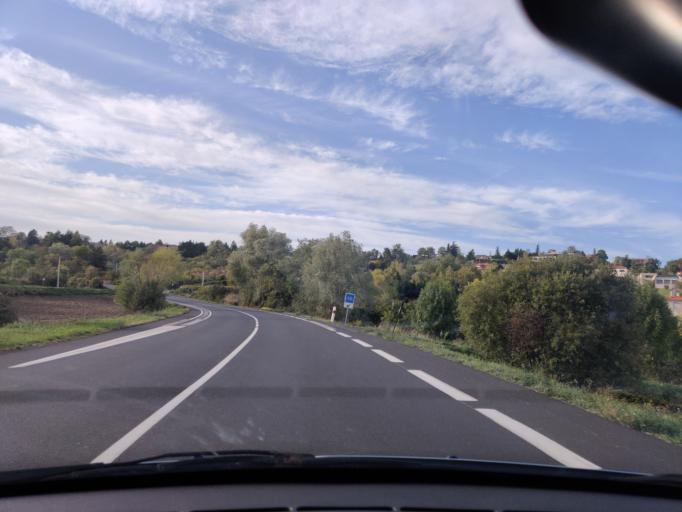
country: FR
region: Auvergne
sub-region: Departement du Puy-de-Dome
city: Mozac
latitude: 45.9070
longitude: 3.0964
